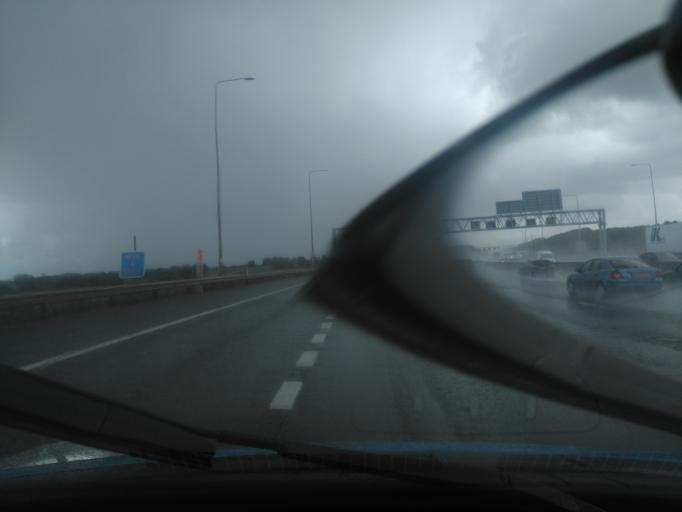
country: GB
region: England
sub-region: Hertfordshire
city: Shenley AV
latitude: 51.7149
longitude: -0.2690
